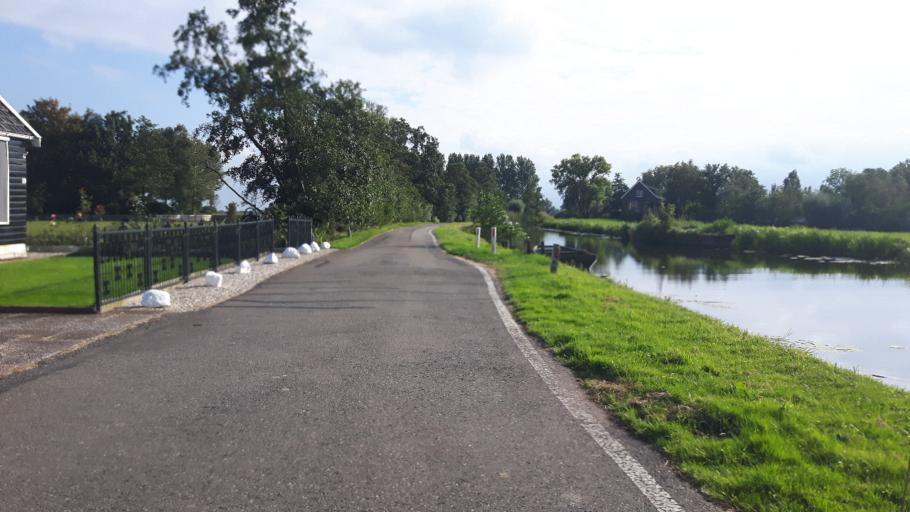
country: NL
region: Utrecht
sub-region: Gemeente De Ronde Venen
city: Mijdrecht
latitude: 52.1788
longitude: 4.9053
